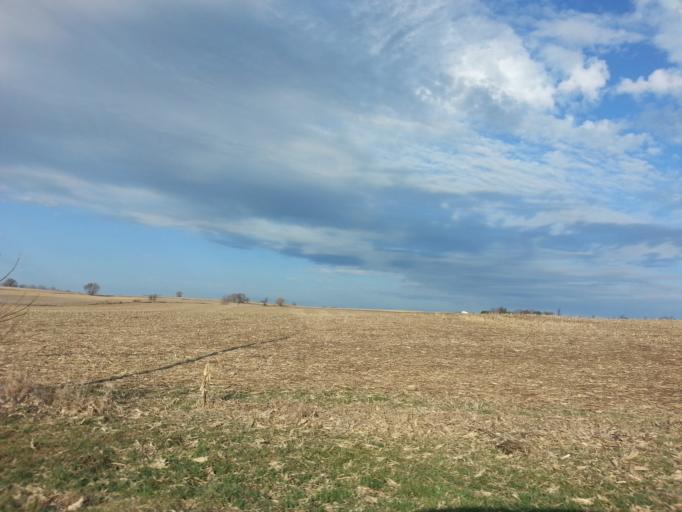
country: US
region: Minnesota
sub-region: Dakota County
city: Hastings
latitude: 44.8270
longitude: -92.8417
